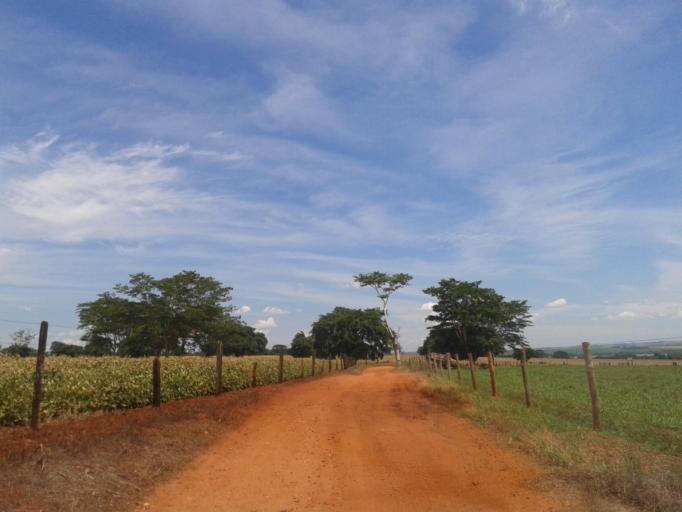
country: BR
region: Minas Gerais
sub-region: Capinopolis
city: Capinopolis
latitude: -18.6502
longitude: -49.7519
